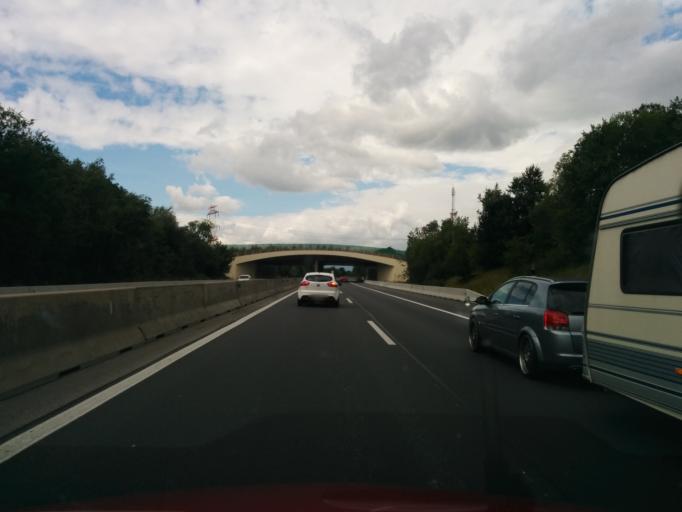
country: AT
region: Lower Austria
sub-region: Politischer Bezirk Ganserndorf
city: Orth an der Donau
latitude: 48.0710
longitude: 16.6867
